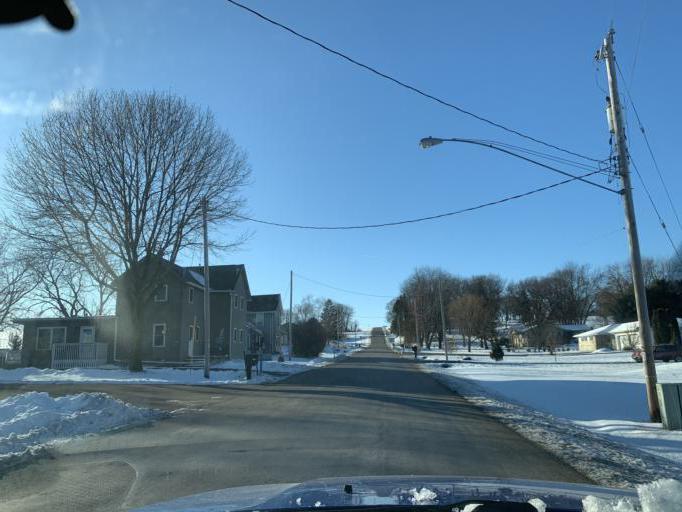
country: US
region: Wisconsin
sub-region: Dane County
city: Cross Plains
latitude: 43.0607
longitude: -89.6569
